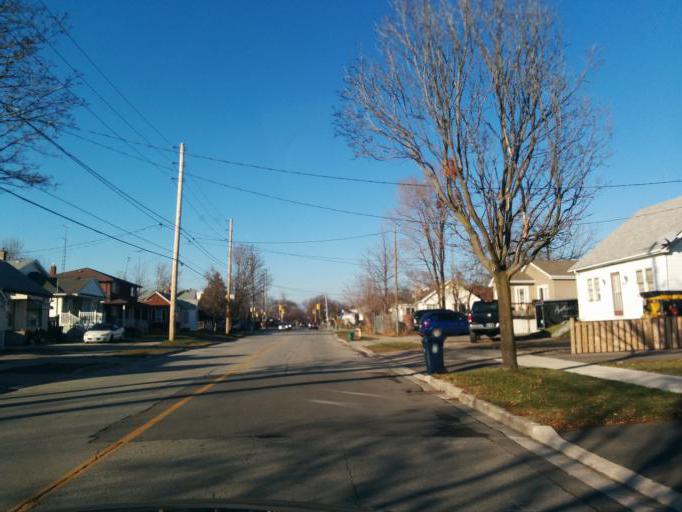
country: CA
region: Ontario
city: Etobicoke
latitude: 43.6028
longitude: -79.5330
